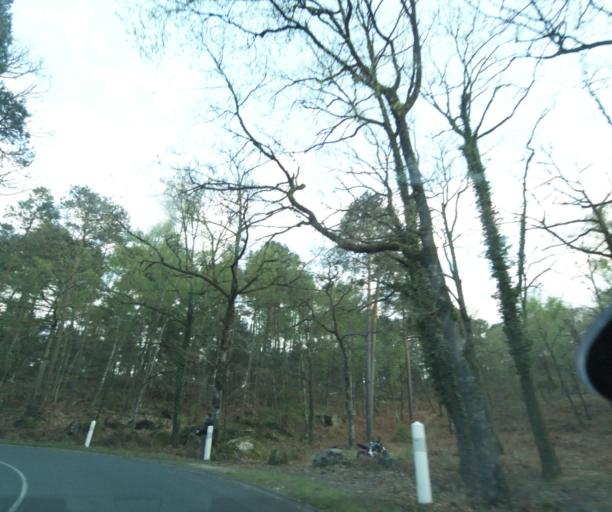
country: FR
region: Ile-de-France
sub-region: Departement de Seine-et-Marne
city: Montigny-sur-Loing
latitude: 48.3535
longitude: 2.7609
